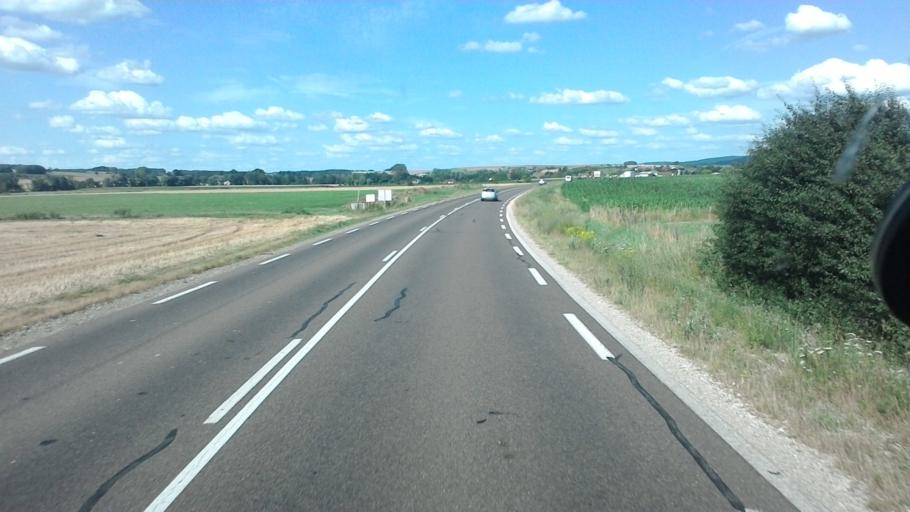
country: FR
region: Franche-Comte
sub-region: Departement de la Haute-Saone
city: Gy
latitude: 47.4183
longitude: 5.8189
